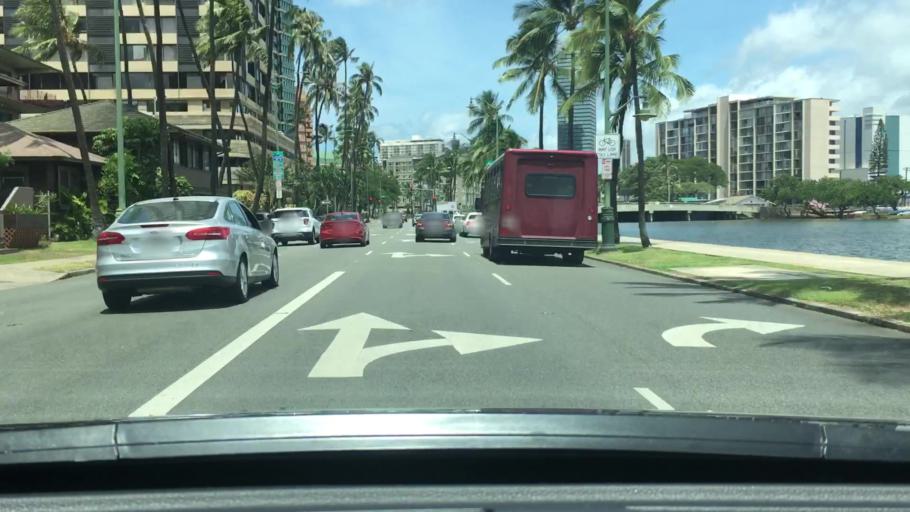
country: US
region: Hawaii
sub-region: Honolulu County
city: Honolulu
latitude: 21.2868
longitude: -157.8317
